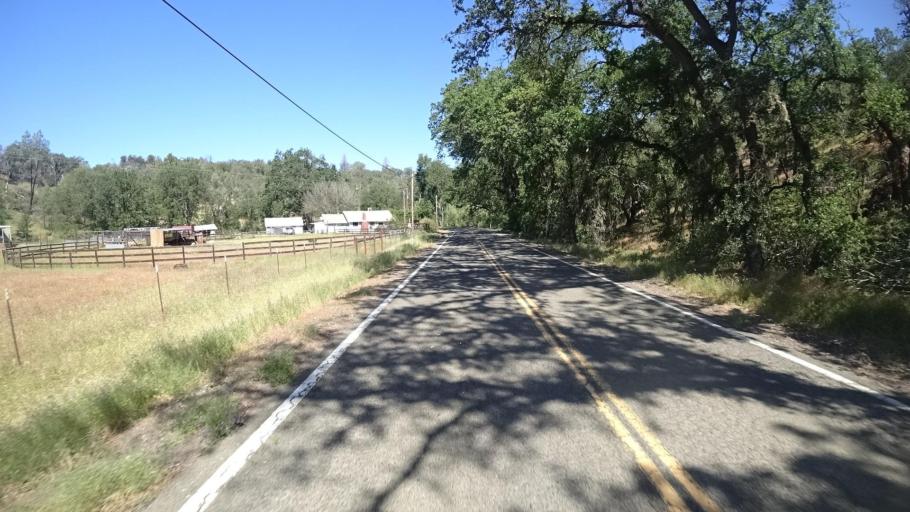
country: US
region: California
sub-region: Lake County
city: Lower Lake
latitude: 38.9040
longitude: -122.5772
